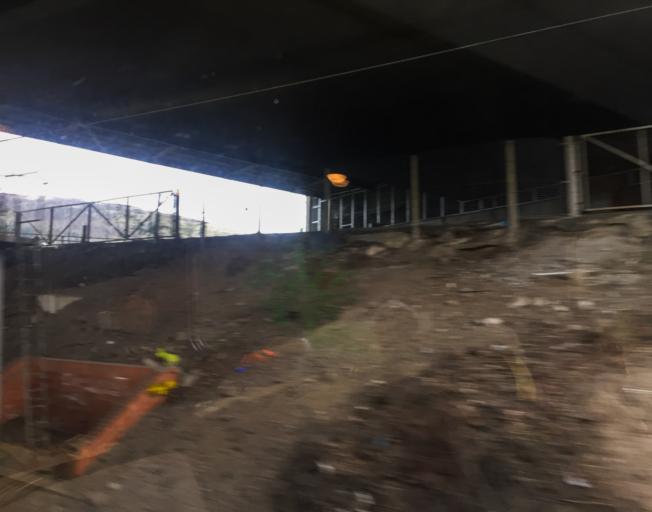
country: GB
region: Scotland
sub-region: West Dunbartonshire
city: Old Kilpatrick
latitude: 55.9231
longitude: -4.4511
